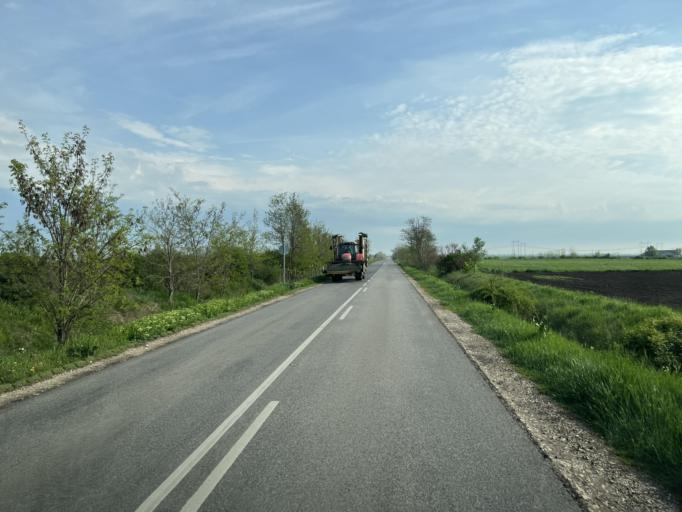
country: HU
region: Pest
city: Cegled
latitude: 47.2265
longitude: 19.7708
